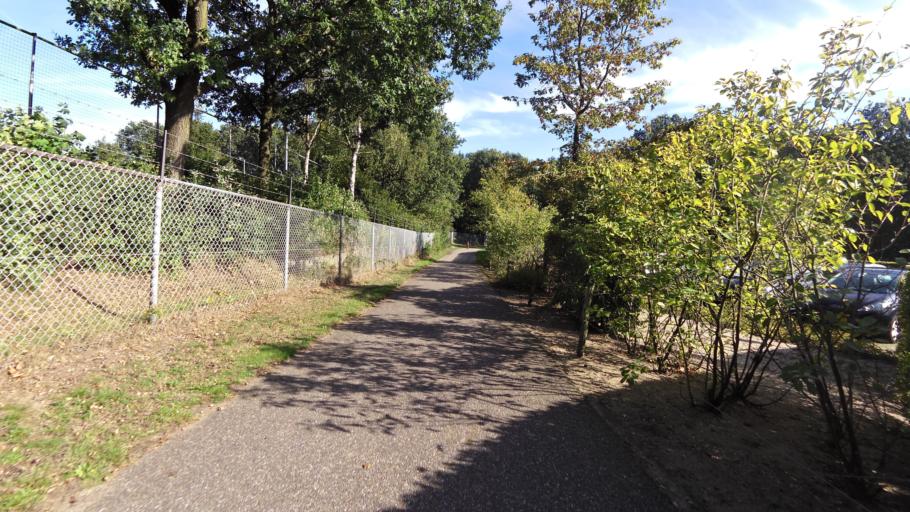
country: NL
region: Gelderland
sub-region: Gemeente Renkum
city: Heelsum
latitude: 51.9879
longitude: 5.7568
